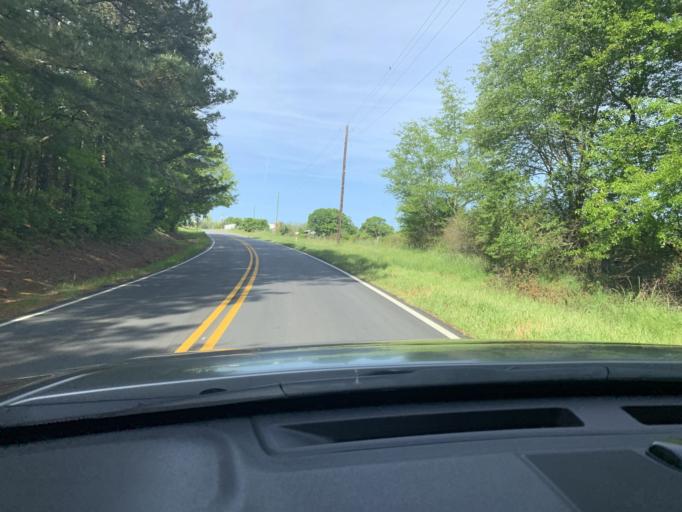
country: US
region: Georgia
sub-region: Oconee County
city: Watkinsville
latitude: 33.8174
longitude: -83.4309
